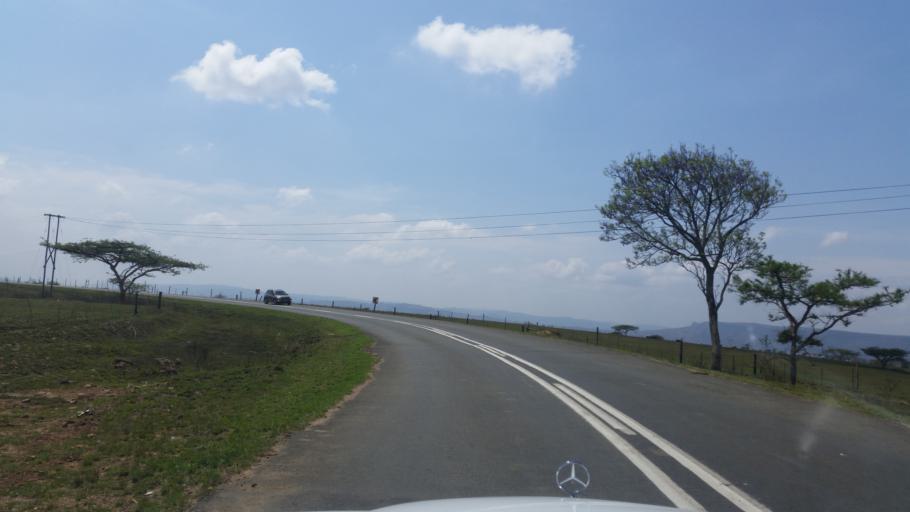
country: ZA
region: KwaZulu-Natal
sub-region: uMgungundlovu District Municipality
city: Camperdown
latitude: -29.6624
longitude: 30.5272
